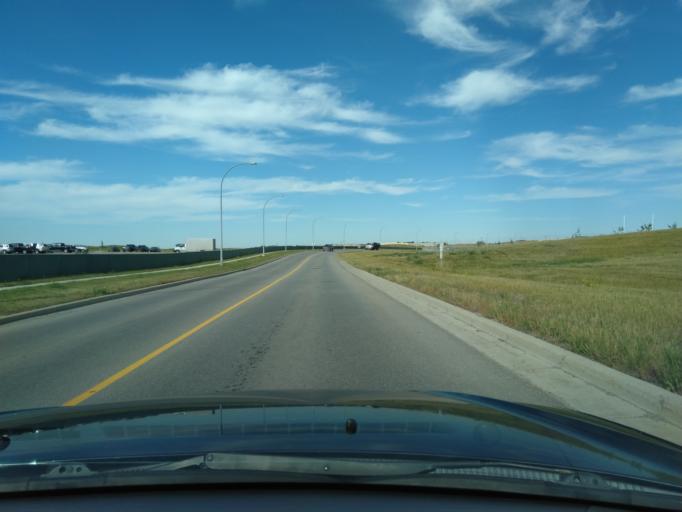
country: CA
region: Alberta
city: Calgary
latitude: 51.0986
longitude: -113.9870
